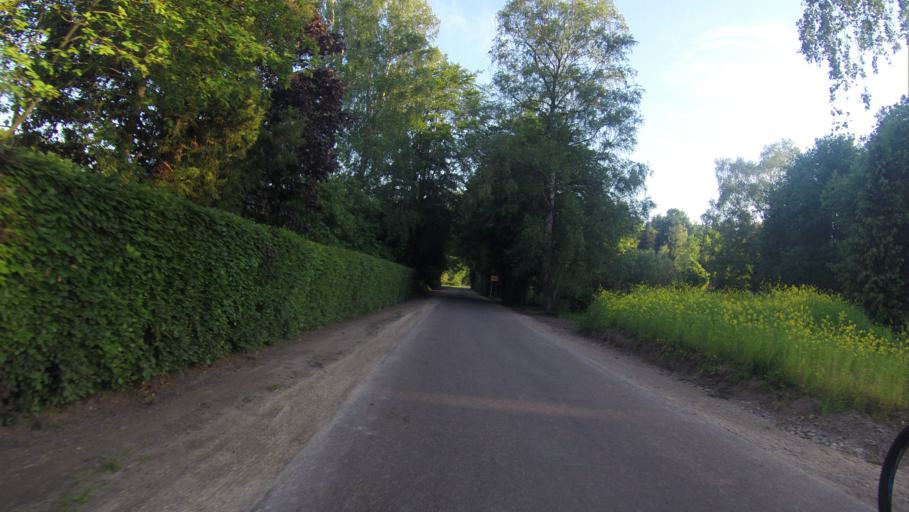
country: NL
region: Gelderland
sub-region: Gemeente Lochem
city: Lochem
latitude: 52.1145
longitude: 6.3765
